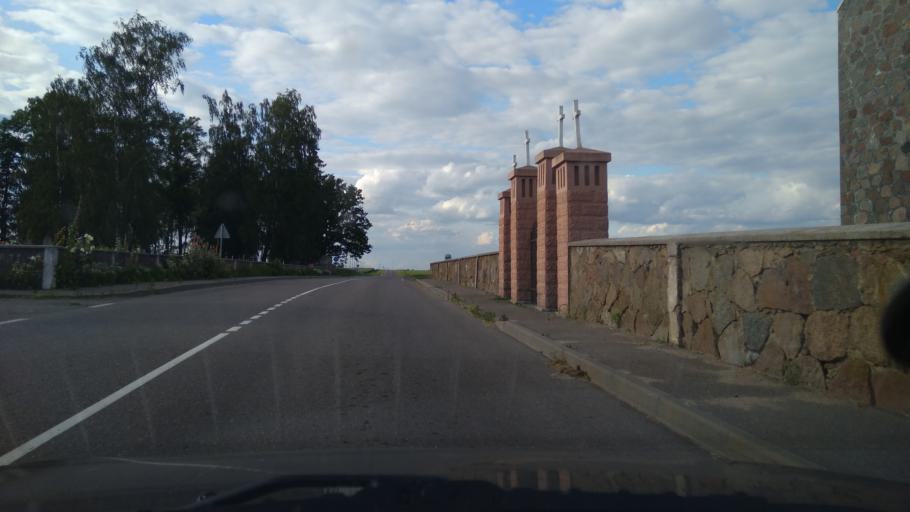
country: BY
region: Grodnenskaya
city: Zel'va
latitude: 53.2746
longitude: 24.6824
